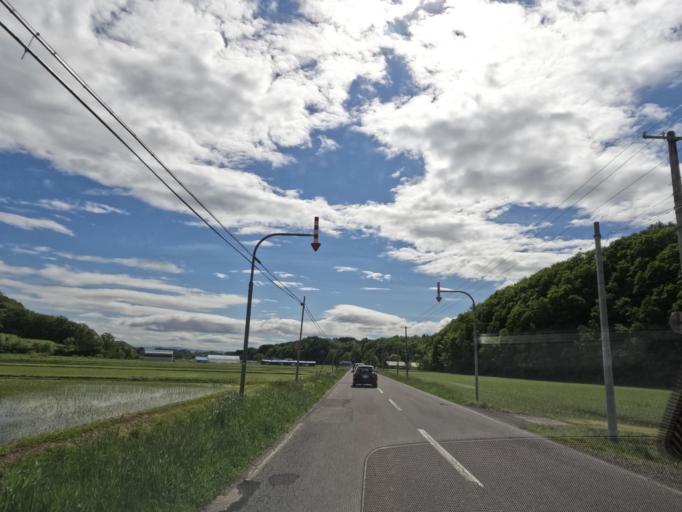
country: JP
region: Hokkaido
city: Kamikawa
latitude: 43.8697
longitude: 142.5694
